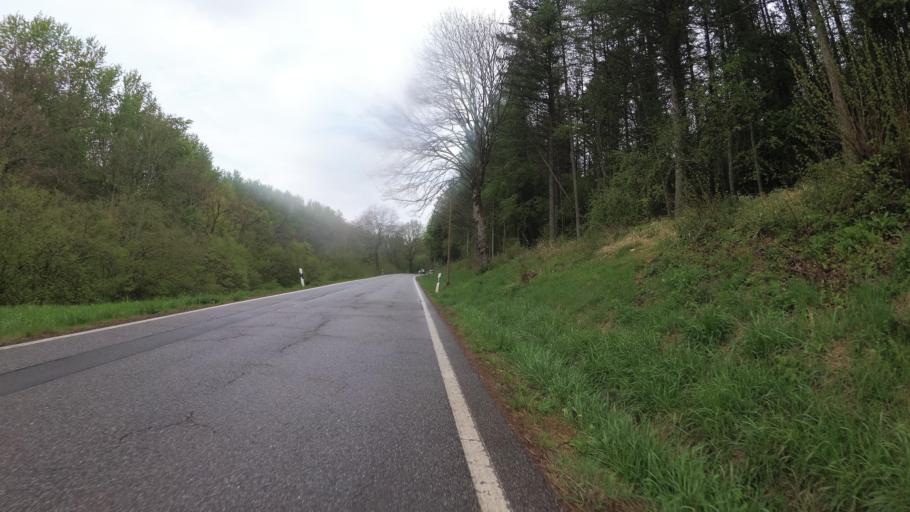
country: FR
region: Lorraine
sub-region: Departement de la Moselle
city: Bouzonville
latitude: 49.3287
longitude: 6.6057
